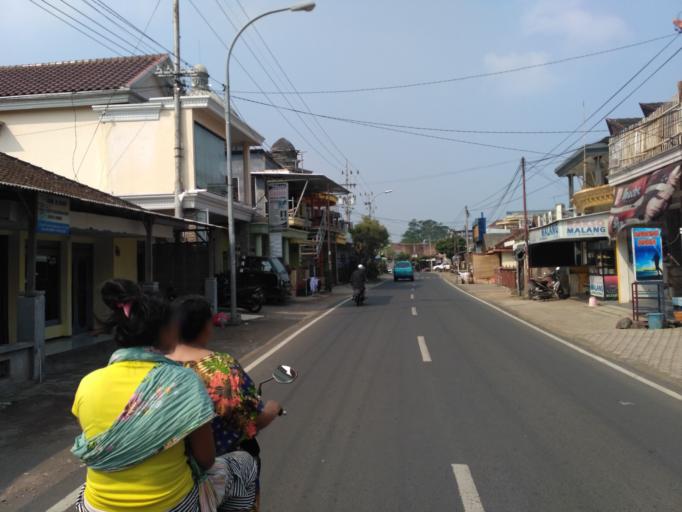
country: ID
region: East Java
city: Batu
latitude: -7.8642
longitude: 112.5517
